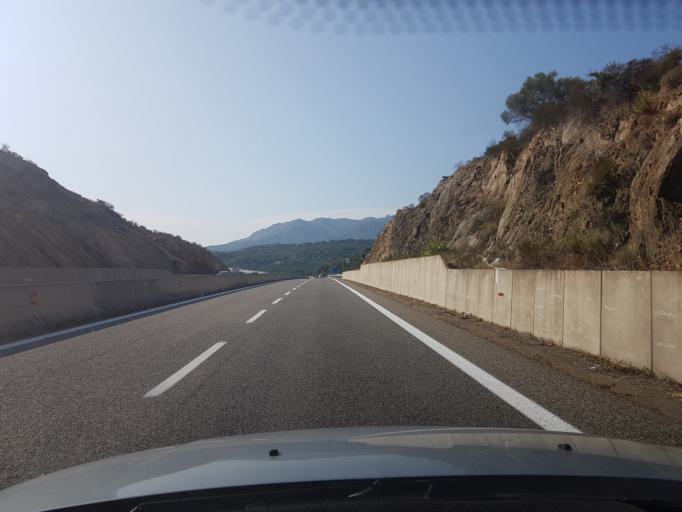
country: IT
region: Sardinia
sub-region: Provincia di Olbia-Tempio
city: Padru
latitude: 40.8218
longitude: 9.5807
